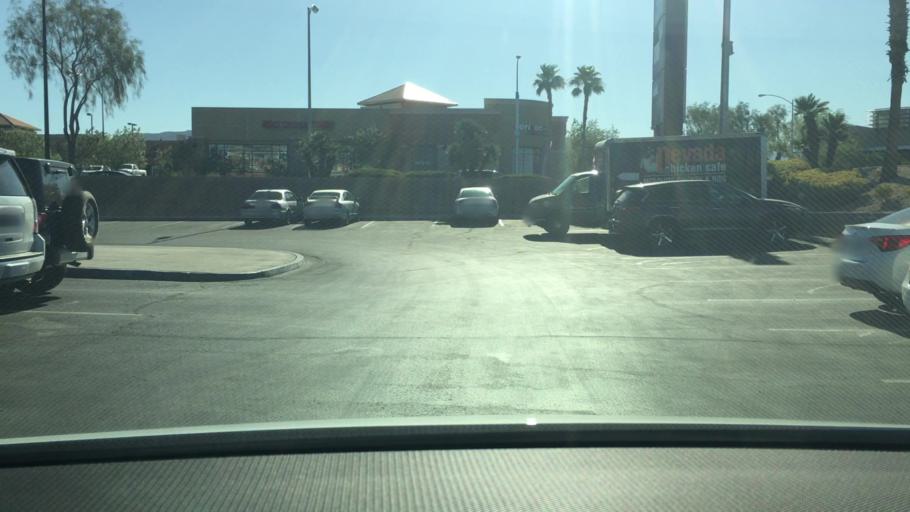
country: US
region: Nevada
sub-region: Clark County
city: Summerlin South
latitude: 36.0961
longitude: -115.2966
